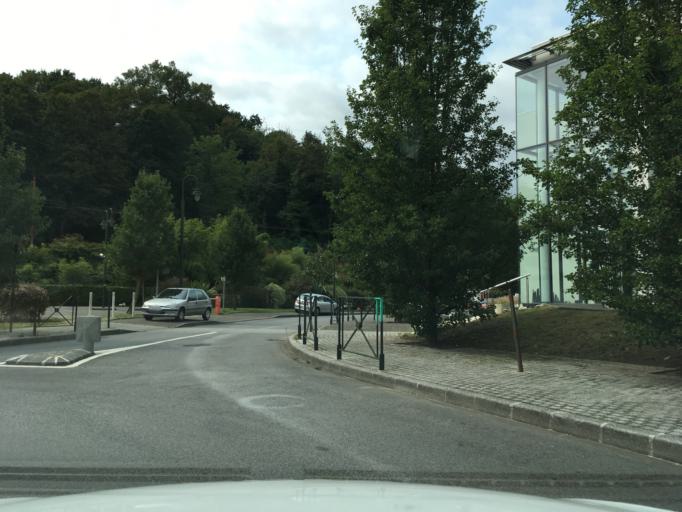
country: FR
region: Aquitaine
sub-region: Departement des Pyrenees-Atlantiques
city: Bayonne
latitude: 43.4848
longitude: -1.4589
